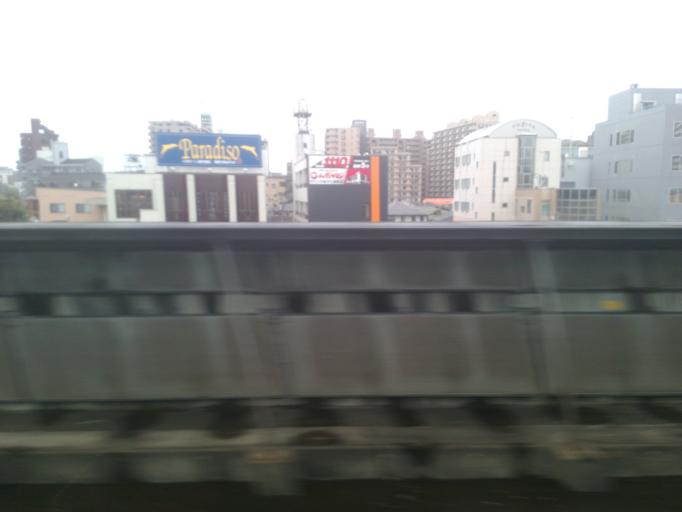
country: JP
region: Miyagi
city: Sendai
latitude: 38.2267
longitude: 140.8854
